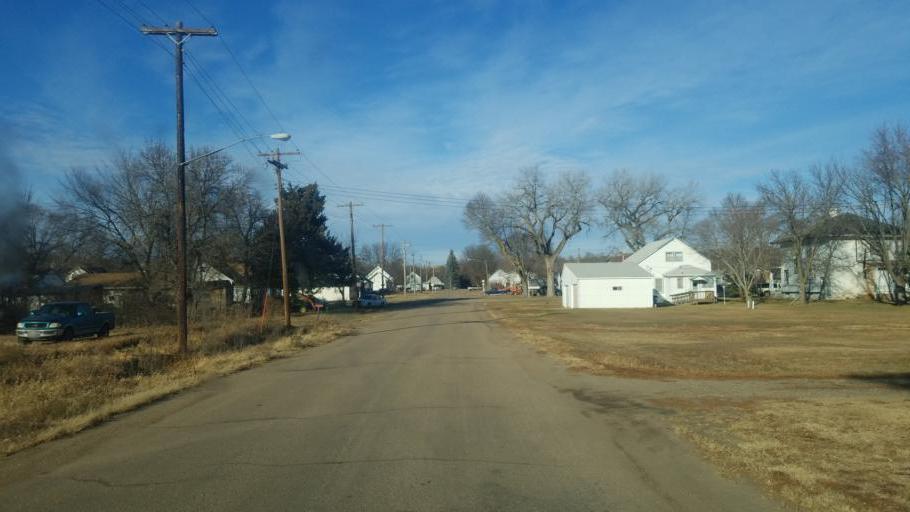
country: US
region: South Dakota
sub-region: Charles Mix County
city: Wagner
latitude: 42.8284
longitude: -98.4682
